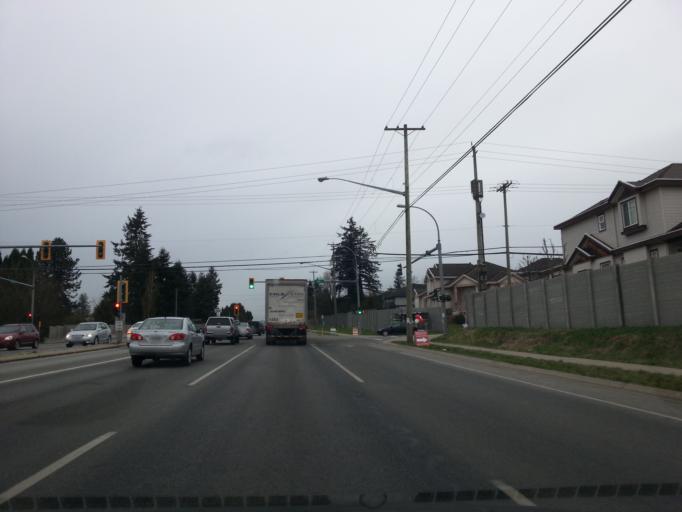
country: CA
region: British Columbia
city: Surrey
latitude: 49.1046
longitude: -122.8116
